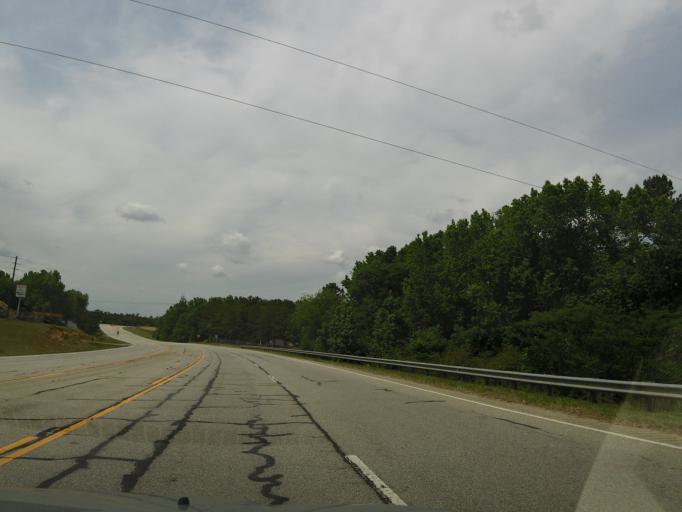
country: US
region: Georgia
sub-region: Jefferson County
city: Wadley
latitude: 32.8852
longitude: -82.3960
